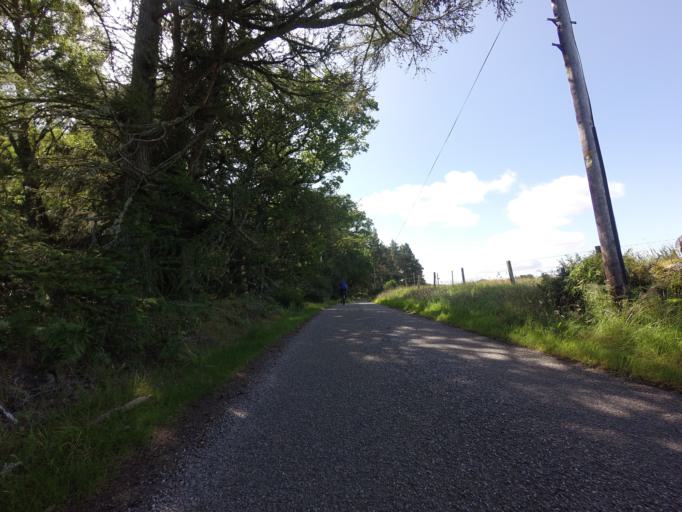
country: GB
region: Scotland
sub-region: Highland
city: Nairn
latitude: 57.5037
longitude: -3.9380
